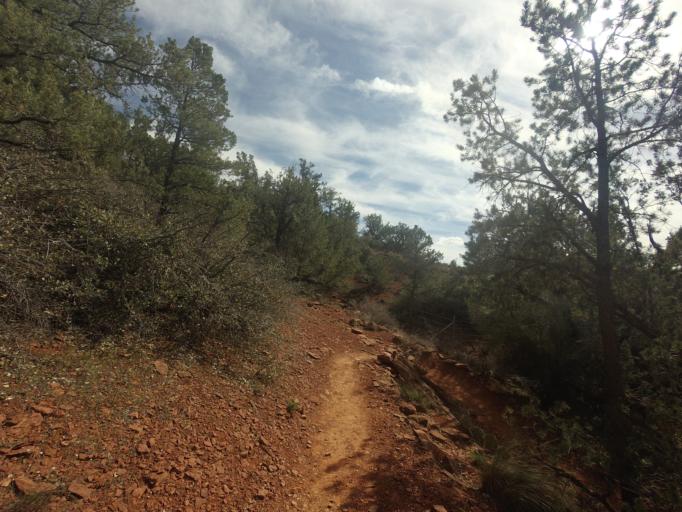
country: US
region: Arizona
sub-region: Yavapai County
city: West Sedona
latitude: 34.8110
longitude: -111.8329
